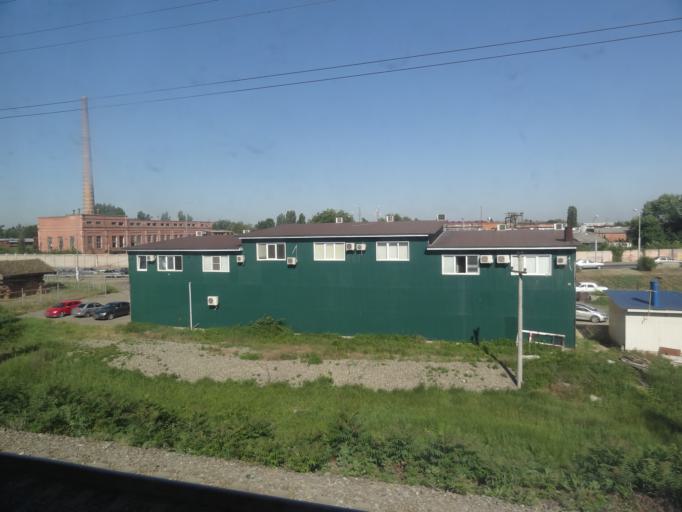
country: RU
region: Adygeya
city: Yablonovskiy
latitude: 44.9916
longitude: 38.9563
